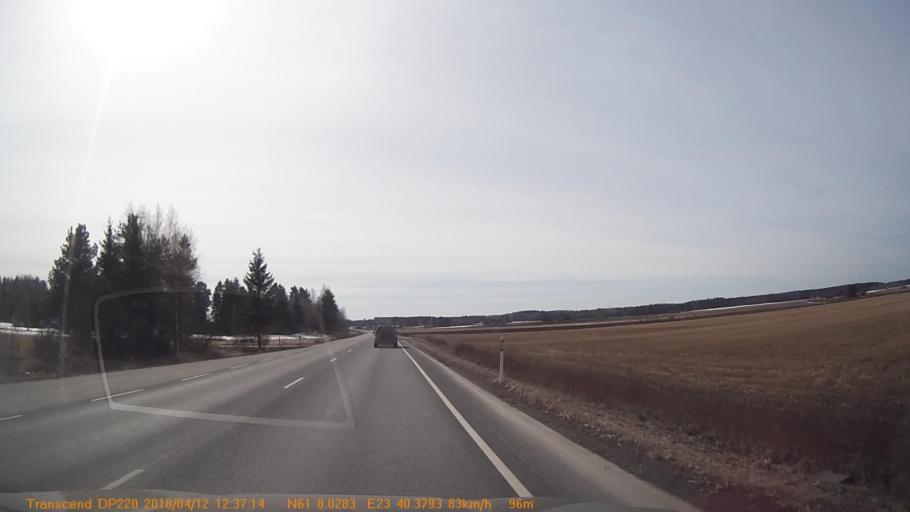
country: FI
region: Pirkanmaa
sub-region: Etelae-Pirkanmaa
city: Kylmaekoski
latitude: 61.1339
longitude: 23.6731
